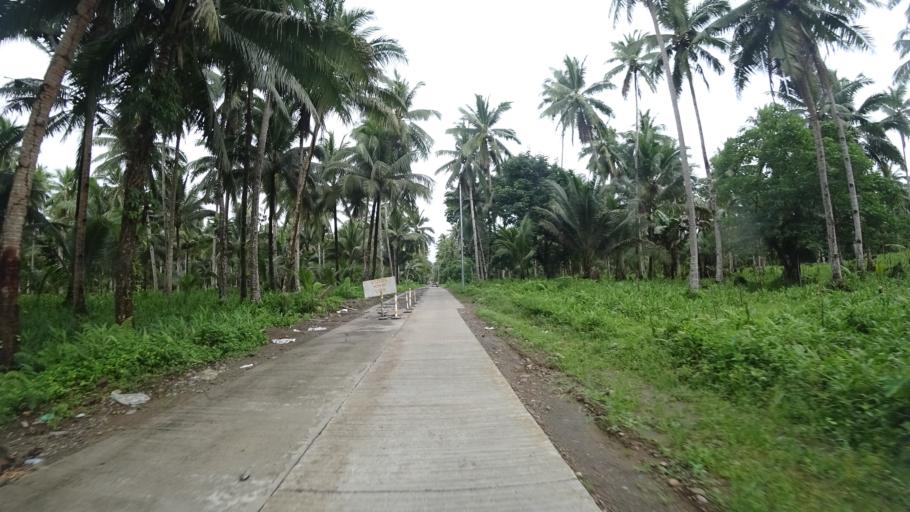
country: PH
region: Eastern Visayas
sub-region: Province of Leyte
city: Bugho
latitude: 10.8257
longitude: 124.9213
